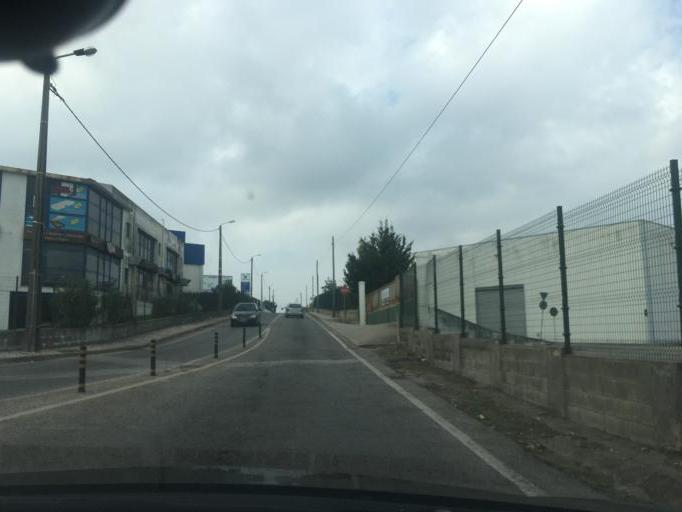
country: PT
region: Lisbon
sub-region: Sintra
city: Sintra
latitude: 38.8350
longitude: -9.3571
